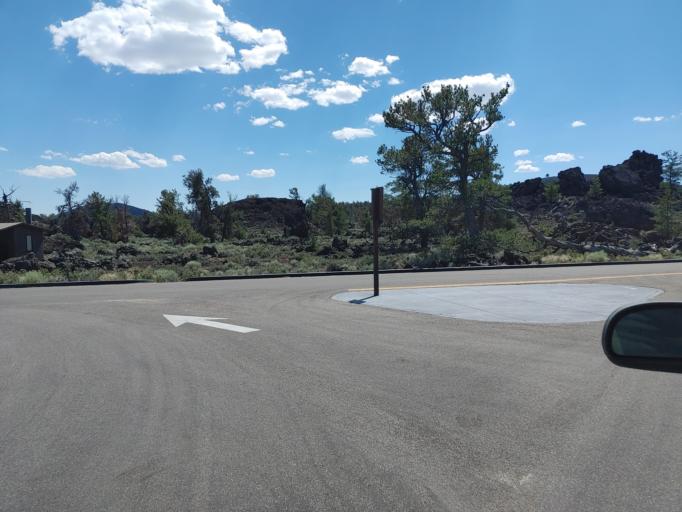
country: US
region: Idaho
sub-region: Butte County
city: Arco
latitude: 43.4516
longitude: -113.5391
